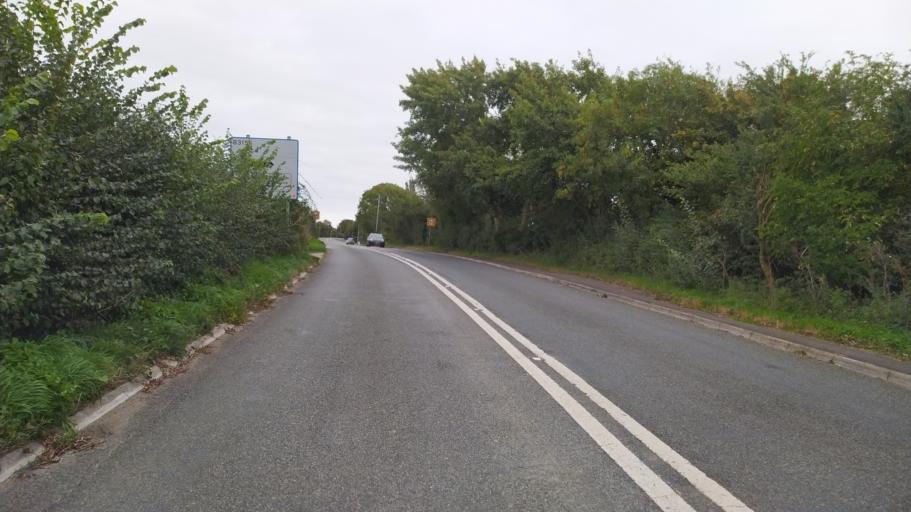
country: GB
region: England
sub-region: Somerset
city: Ilchester
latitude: 51.0117
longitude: -2.6575
